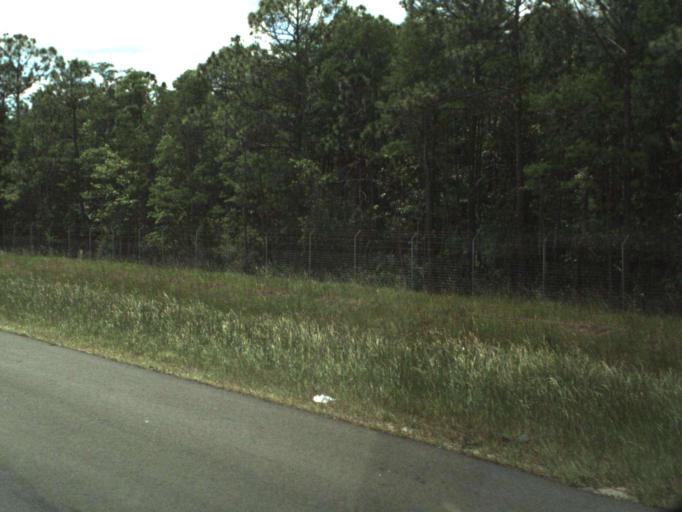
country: US
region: Florida
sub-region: Volusia County
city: Samsula-Spruce Creek
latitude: 29.1075
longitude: -81.1469
